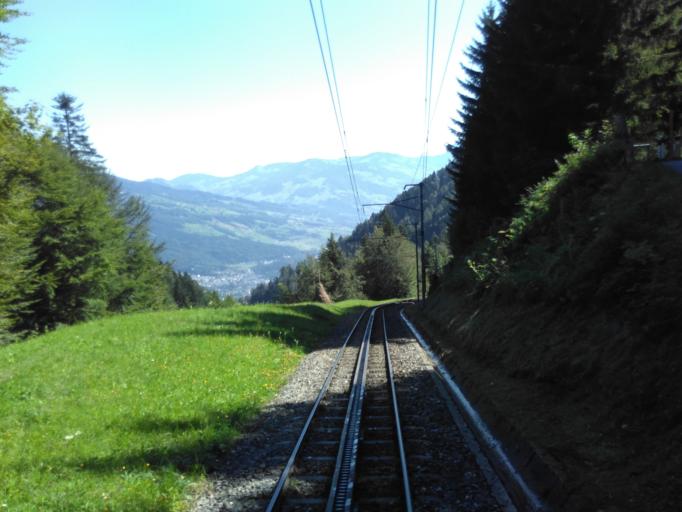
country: CH
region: Schwyz
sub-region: Bezirk Schwyz
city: Arth
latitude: 47.0382
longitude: 8.5077
